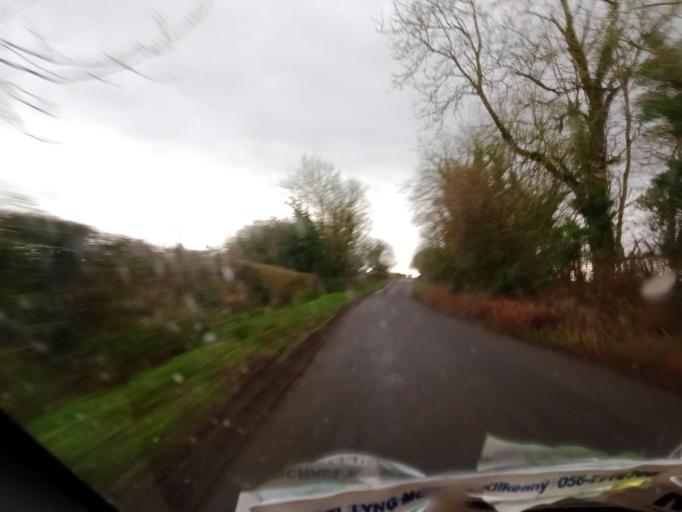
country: IE
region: Munster
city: Fethard
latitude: 52.5457
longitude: -7.7611
